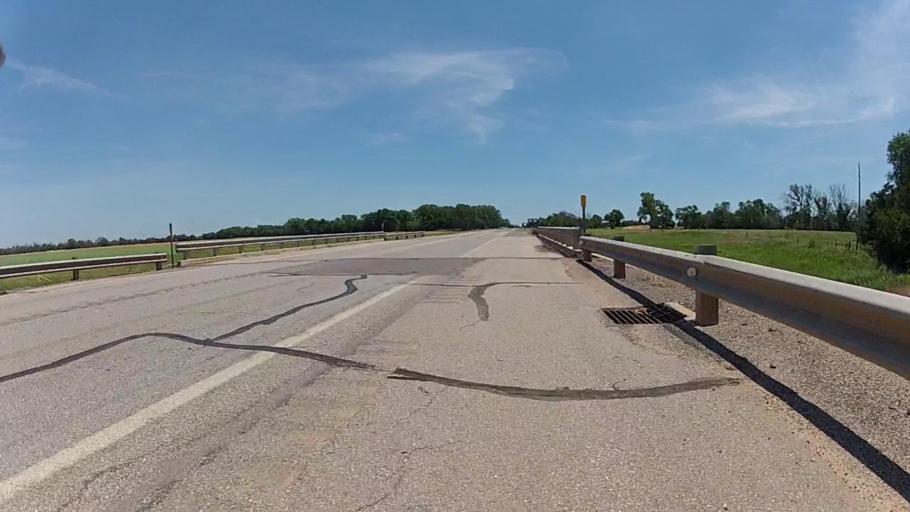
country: US
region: Kansas
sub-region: Barber County
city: Medicine Lodge
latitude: 37.2536
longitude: -98.4151
